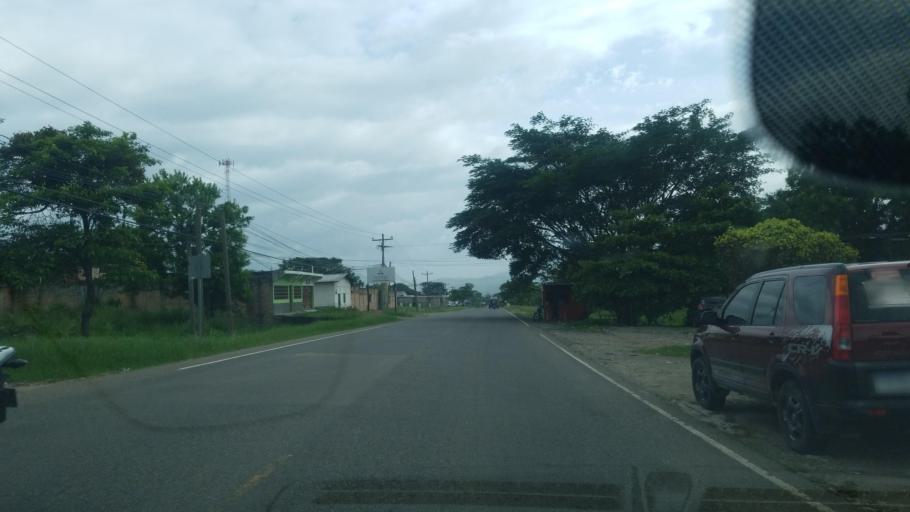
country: HN
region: Ocotepeque
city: Nueva Ocotepeque
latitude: 14.4271
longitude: -89.1834
